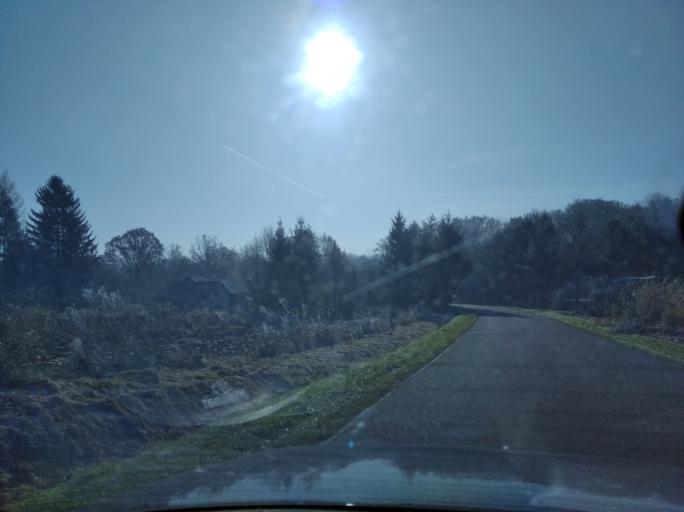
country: PL
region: Subcarpathian Voivodeship
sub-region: Powiat strzyzowski
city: Wysoka Strzyzowska
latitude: 49.8352
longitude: 21.7133
